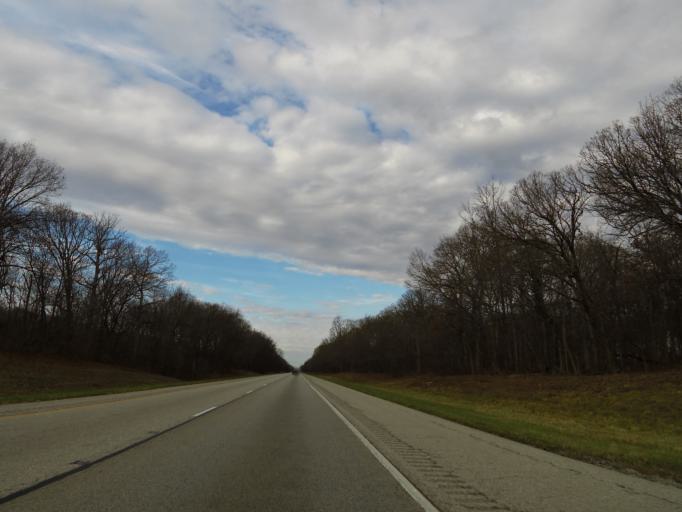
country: US
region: Illinois
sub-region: Washington County
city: Nashville
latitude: 38.4088
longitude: -89.4148
